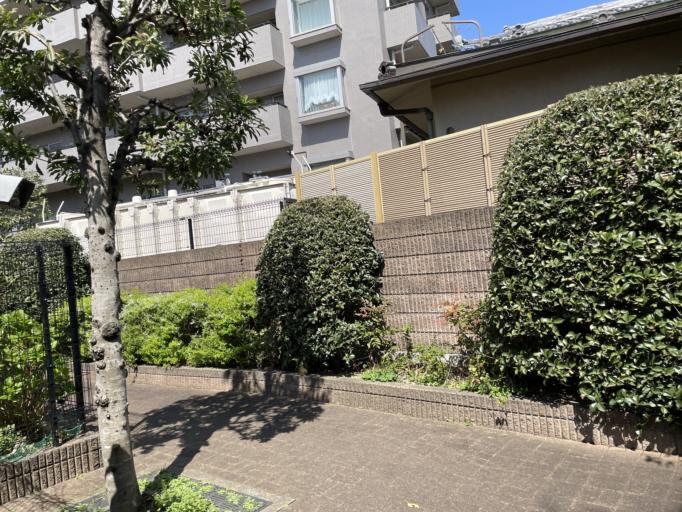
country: JP
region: Tokyo
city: Tokyo
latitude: 35.7078
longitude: 139.6772
